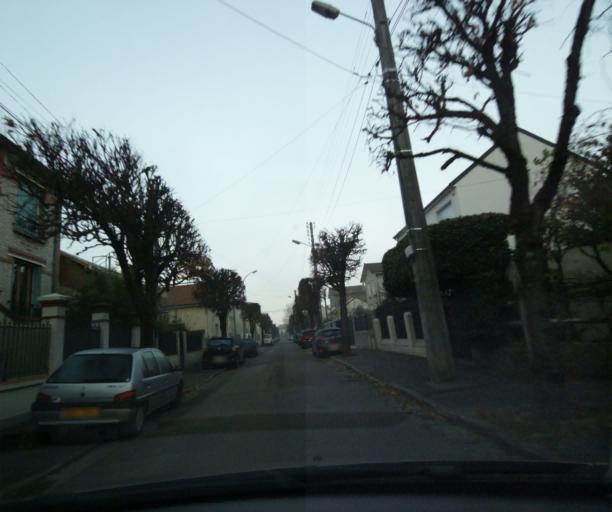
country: FR
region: Ile-de-France
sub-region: Departement de Seine-Saint-Denis
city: Neuilly-Plaisance
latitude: 48.8578
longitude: 2.5094
